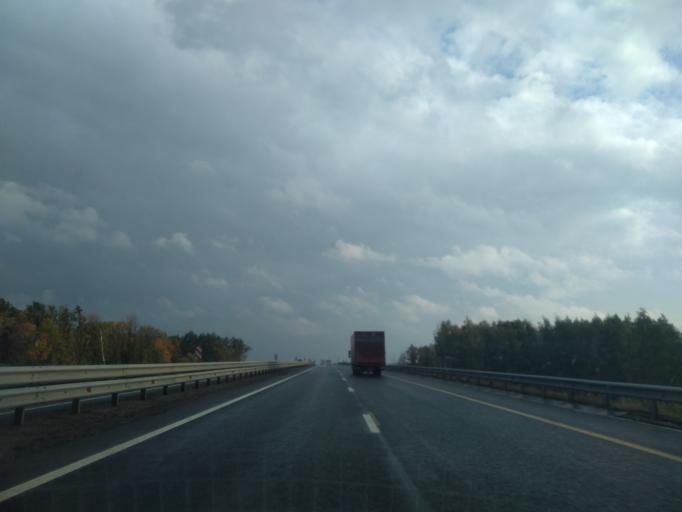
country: RU
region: Lipetsk
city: Yelets
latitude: 52.5960
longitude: 38.6722
